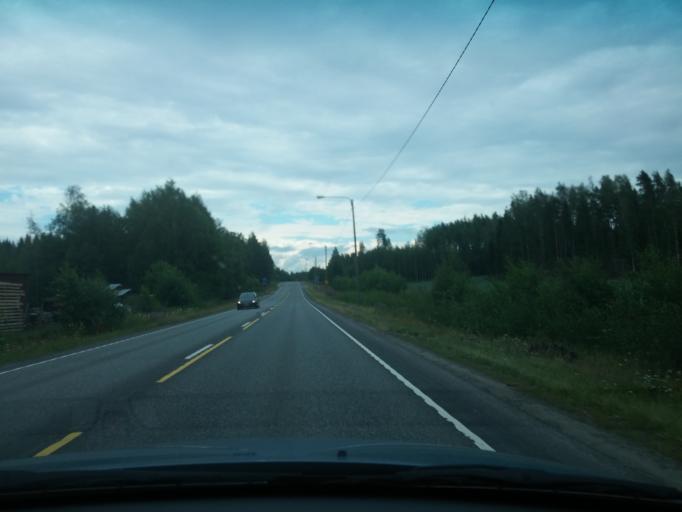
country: FI
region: Haeme
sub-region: Riihimaeki
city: Loppi
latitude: 60.7291
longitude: 24.5249
